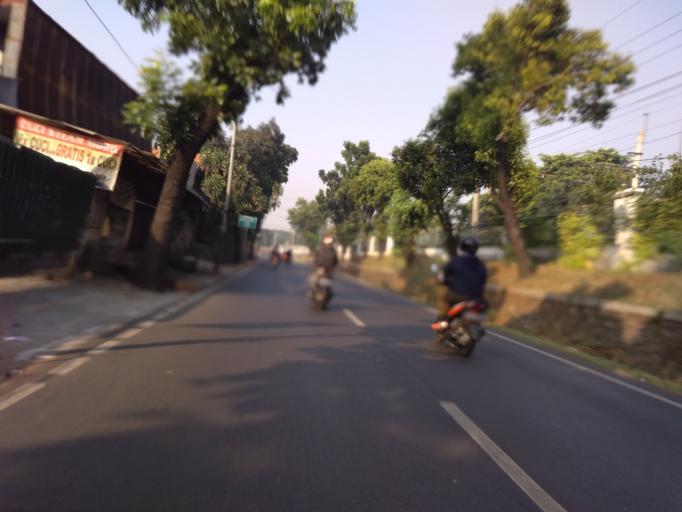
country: ID
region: Jakarta Raya
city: Jakarta
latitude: -6.2937
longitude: 106.8415
